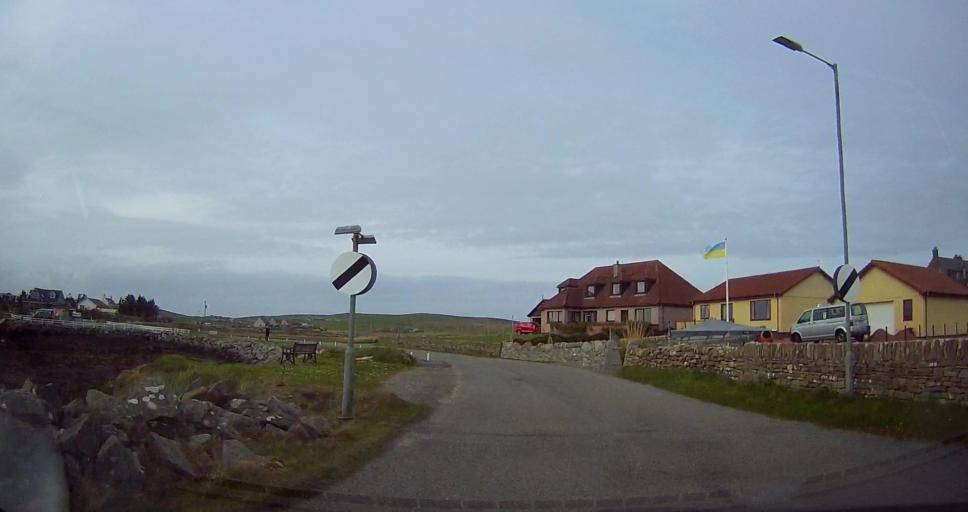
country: GB
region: Scotland
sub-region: Shetland Islands
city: Shetland
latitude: 60.1505
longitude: -1.1138
